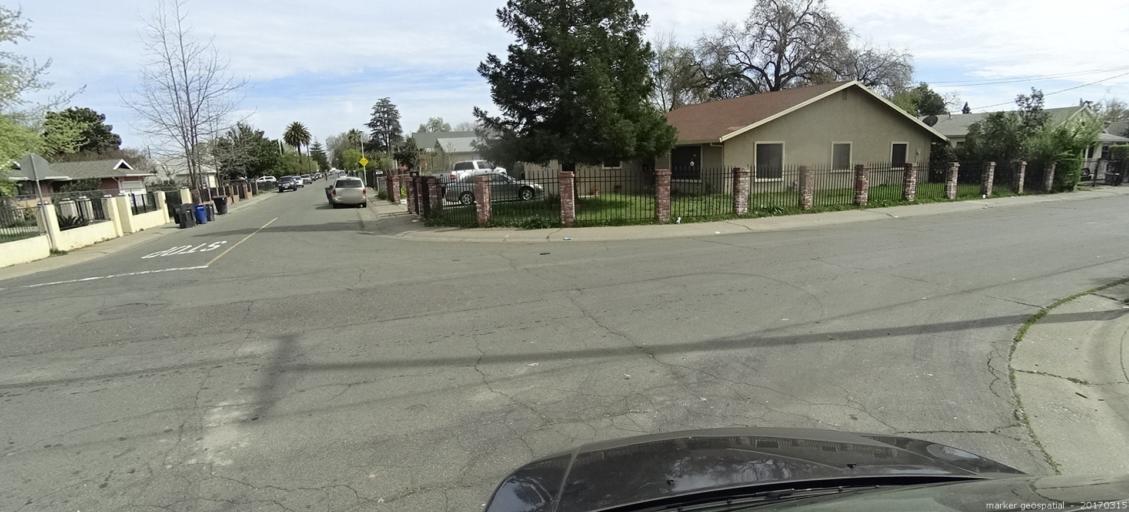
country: US
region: California
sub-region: Sacramento County
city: Parkway
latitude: 38.5236
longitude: -121.4774
